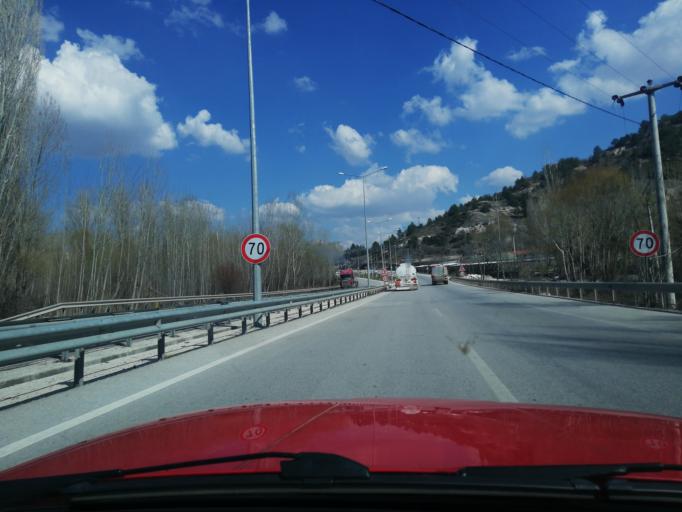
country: TR
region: Burdur
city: Burdur
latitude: 37.6983
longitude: 30.3345
